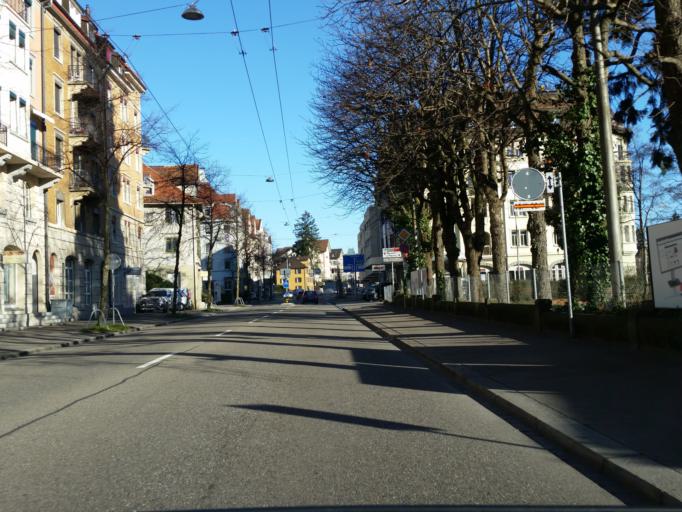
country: CH
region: Saint Gallen
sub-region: Wahlkreis St. Gallen
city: Sankt Gallen
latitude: 47.4332
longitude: 9.3836
